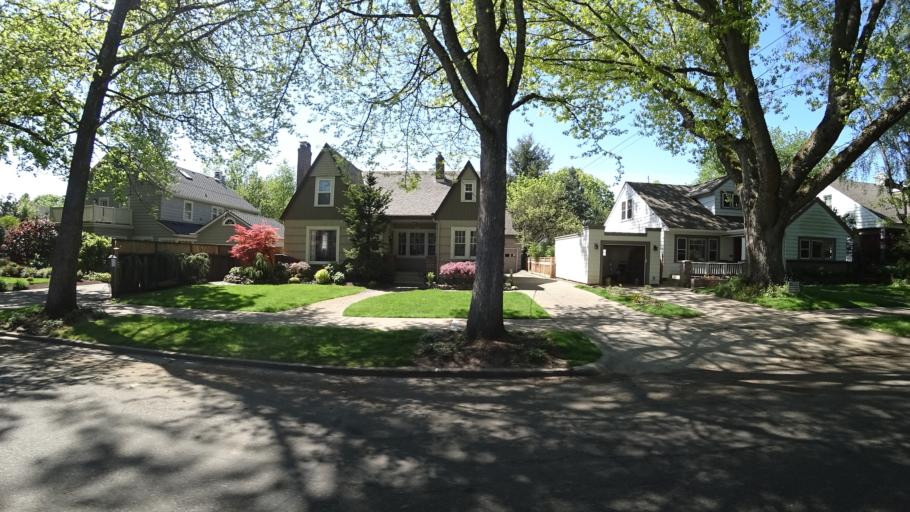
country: US
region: Oregon
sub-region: Clackamas County
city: Milwaukie
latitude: 45.4710
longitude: -122.6263
